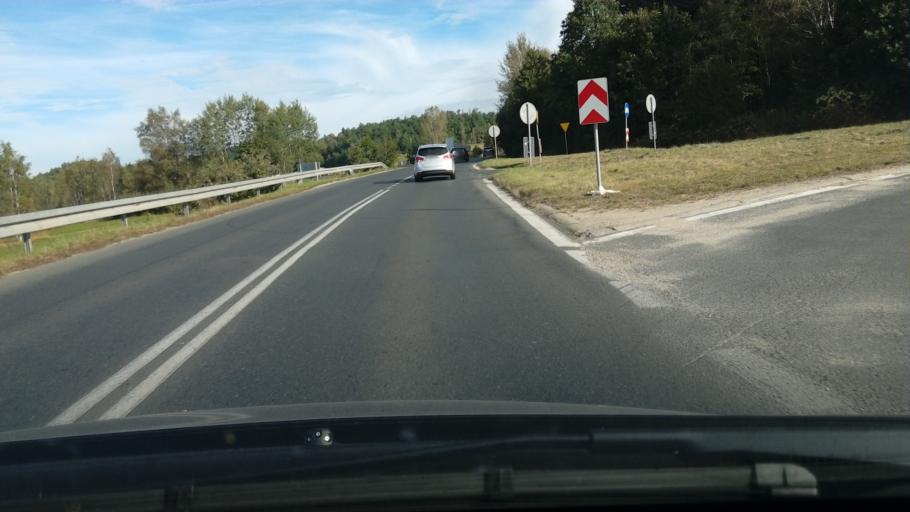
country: PL
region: Lower Silesian Voivodeship
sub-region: Powiat jeleniogorski
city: Myslakowice
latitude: 50.8599
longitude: 15.7738
